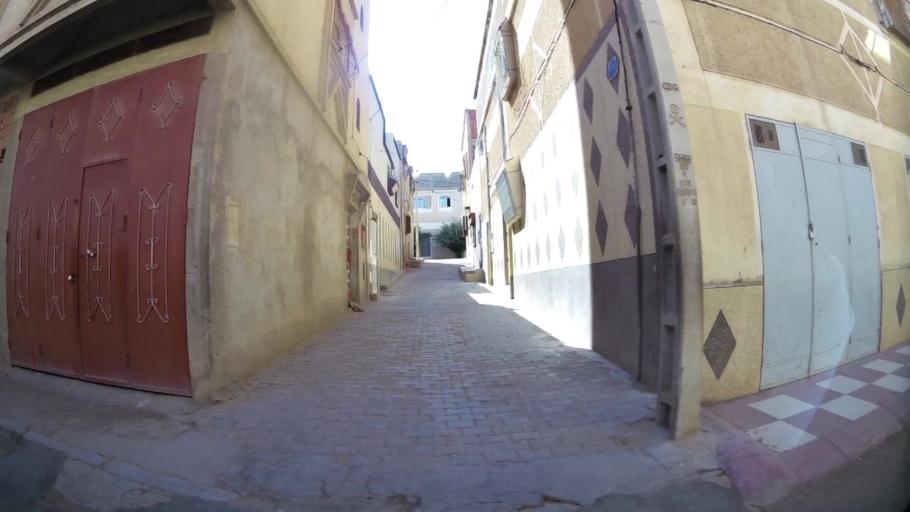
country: MA
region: Oriental
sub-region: Oujda-Angad
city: Oujda
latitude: 34.6893
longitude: -1.9278
